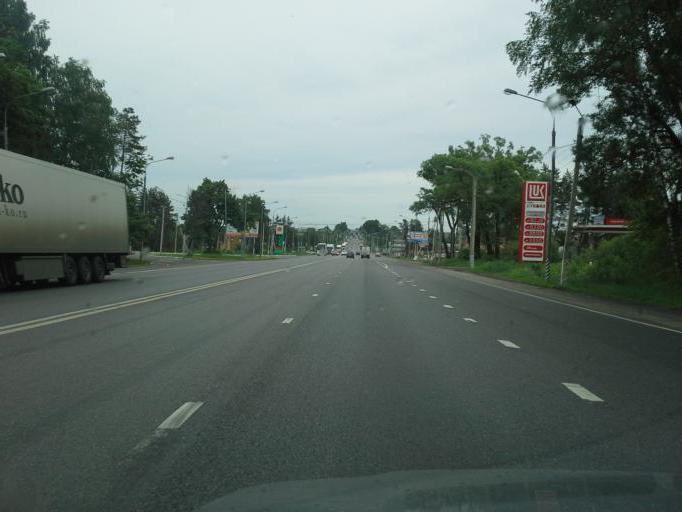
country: RU
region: Vladimir
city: Pokrov
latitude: 55.9141
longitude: 39.1504
